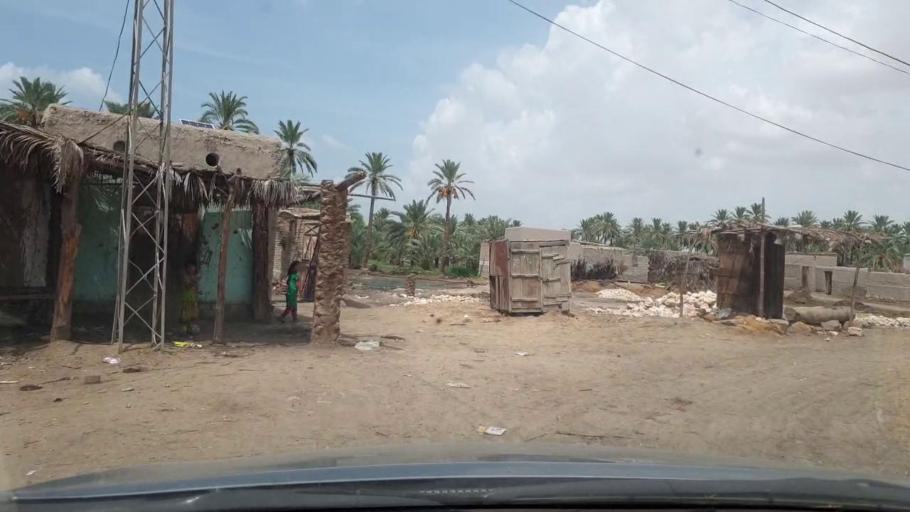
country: PK
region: Sindh
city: Khairpur
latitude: 27.4529
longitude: 68.8219
